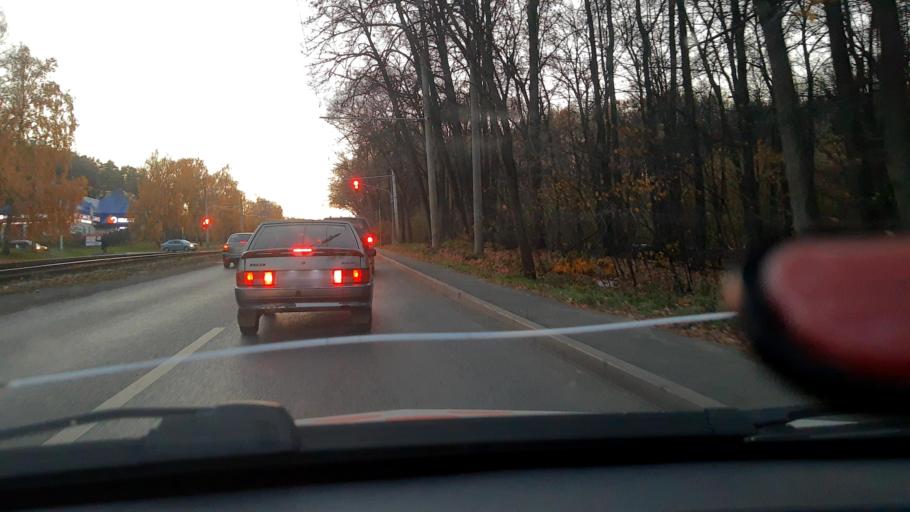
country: RU
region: Bashkortostan
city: Ufa
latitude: 54.7965
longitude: 56.0455
